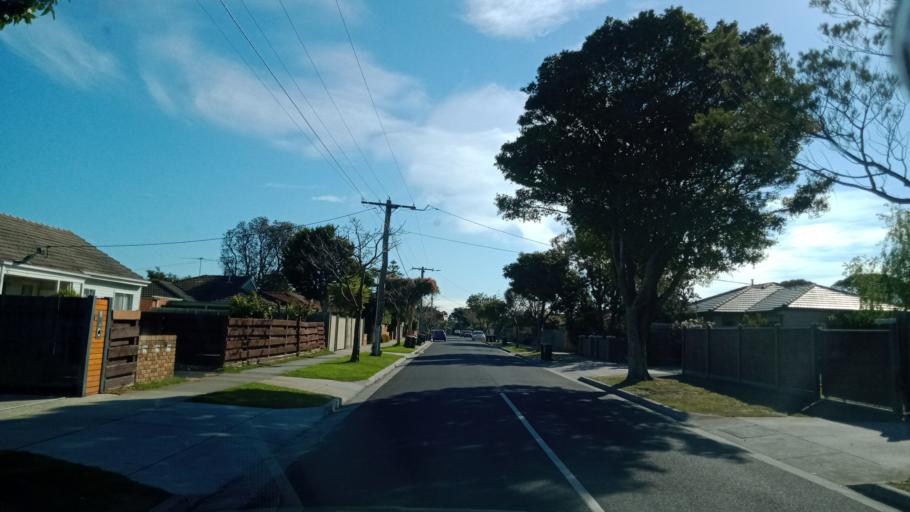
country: AU
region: Victoria
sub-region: Kingston
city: Chelsea
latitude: -38.0434
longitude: 145.1211
